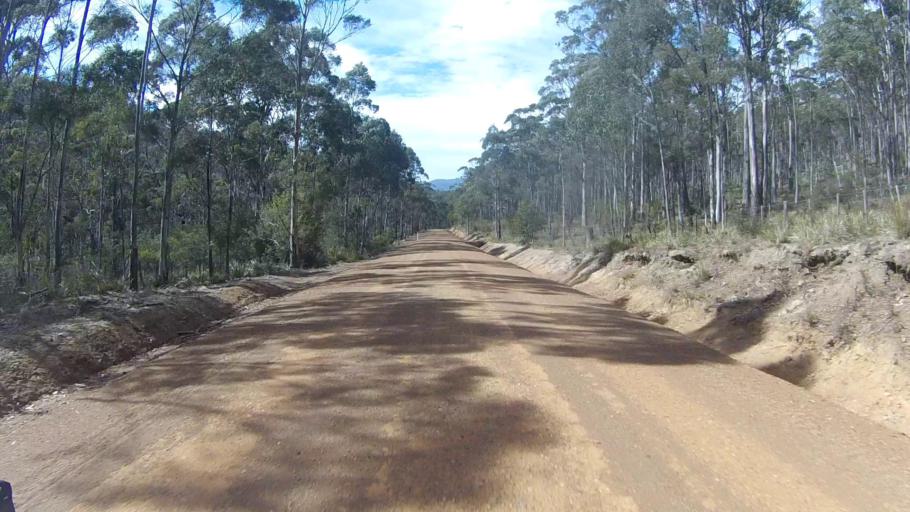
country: AU
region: Tasmania
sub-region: Sorell
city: Sorell
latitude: -42.6195
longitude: 147.9017
